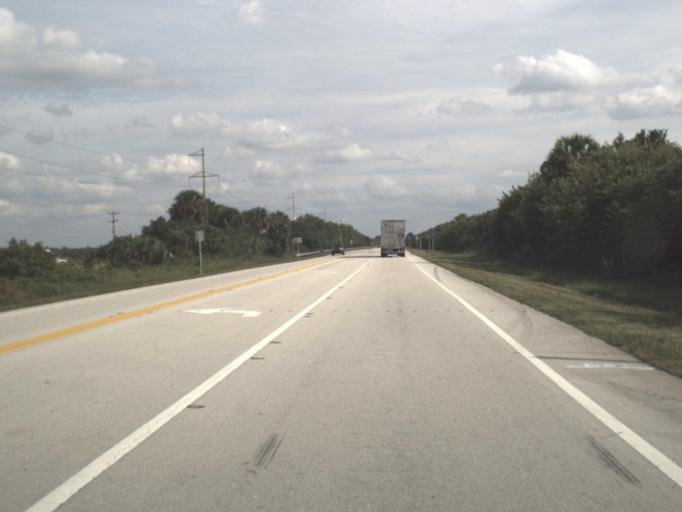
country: US
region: Florida
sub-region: Okeechobee County
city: Taylor Creek
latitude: 27.1601
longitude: -80.6791
